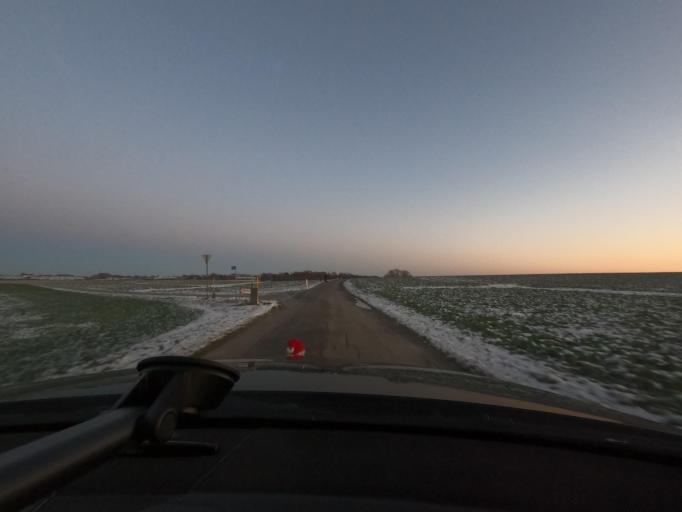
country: DK
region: South Denmark
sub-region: Sonderborg Kommune
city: Horuphav
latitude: 54.8669
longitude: 9.9008
